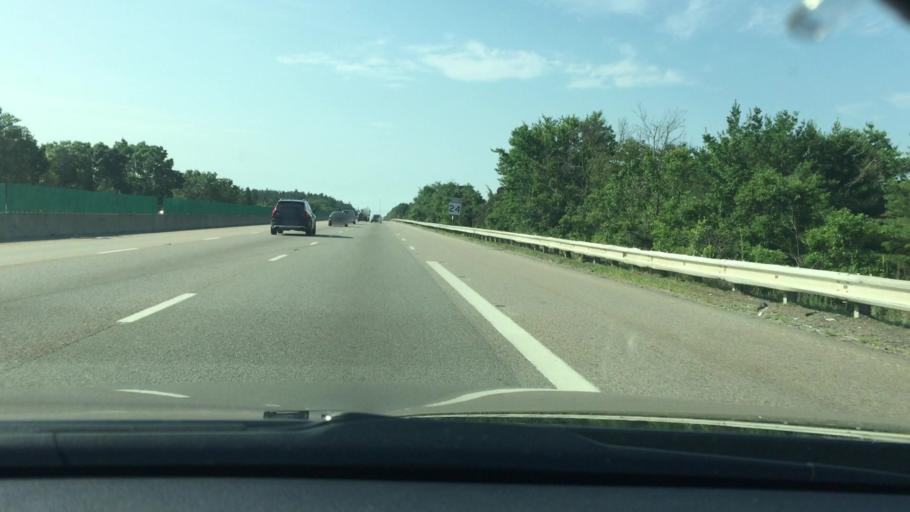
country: US
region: Massachusetts
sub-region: Plymouth County
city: Brockton
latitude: 42.0586
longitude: -71.0610
